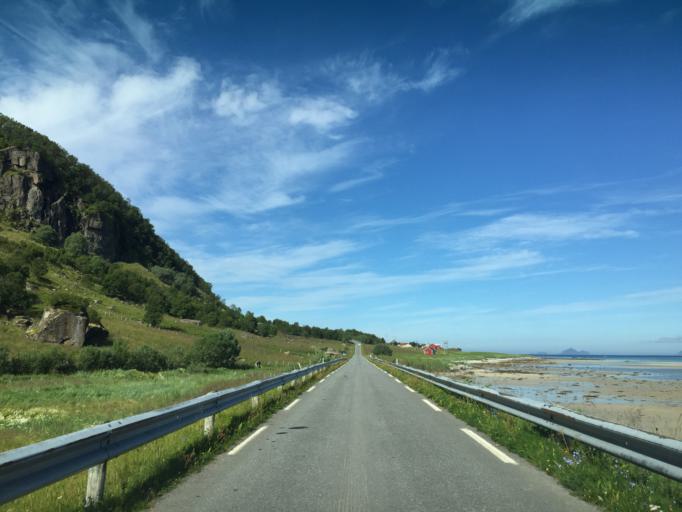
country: NO
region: Nordland
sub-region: Vagan
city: Svolvaer
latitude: 68.3969
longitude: 14.5342
